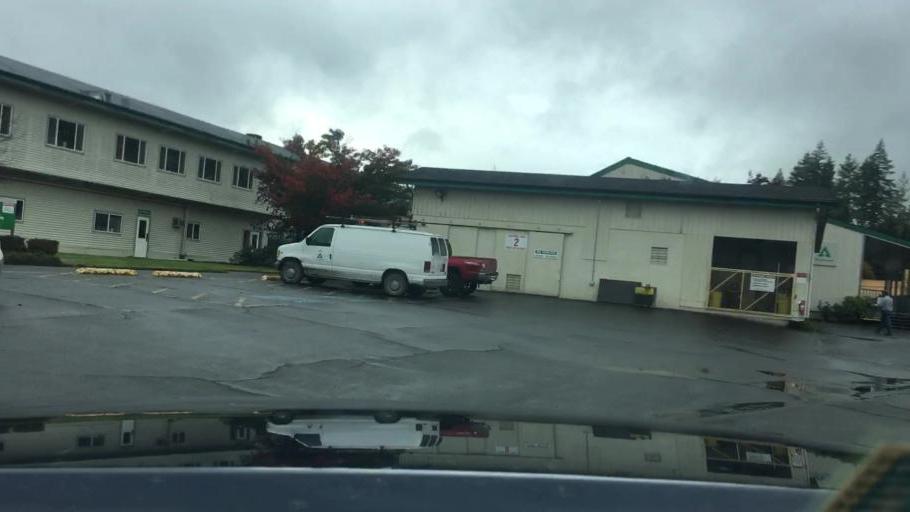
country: US
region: Oregon
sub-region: Lane County
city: Cottage Grove
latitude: 43.7667
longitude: -123.0799
